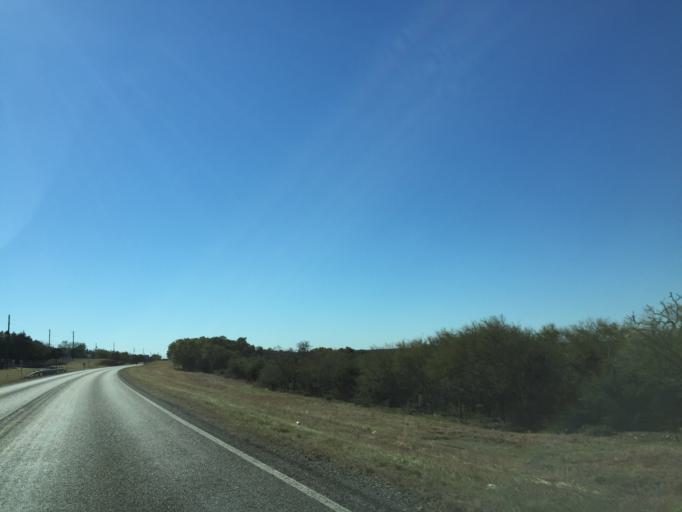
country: US
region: Texas
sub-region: Comal County
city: Garden Ridge
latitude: 29.7511
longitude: -98.3039
